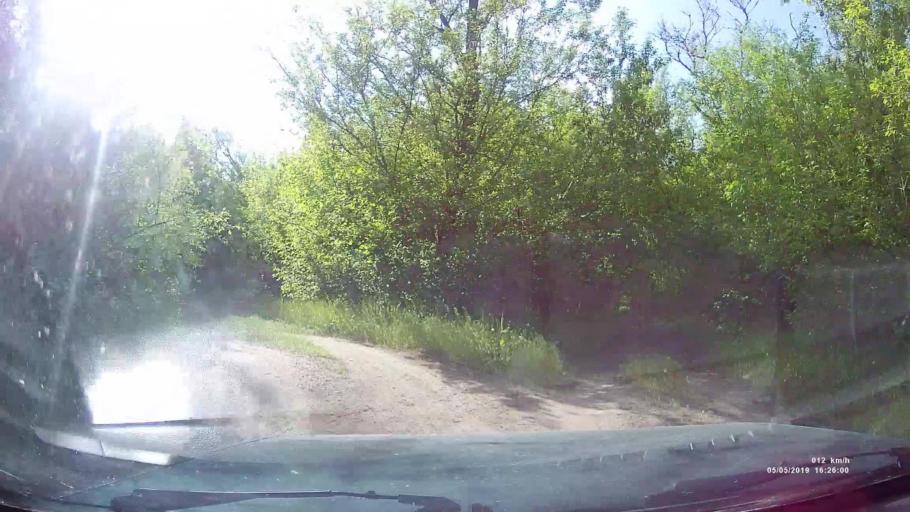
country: RU
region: Rostov
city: Ust'-Donetskiy
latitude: 47.7625
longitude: 41.0223
